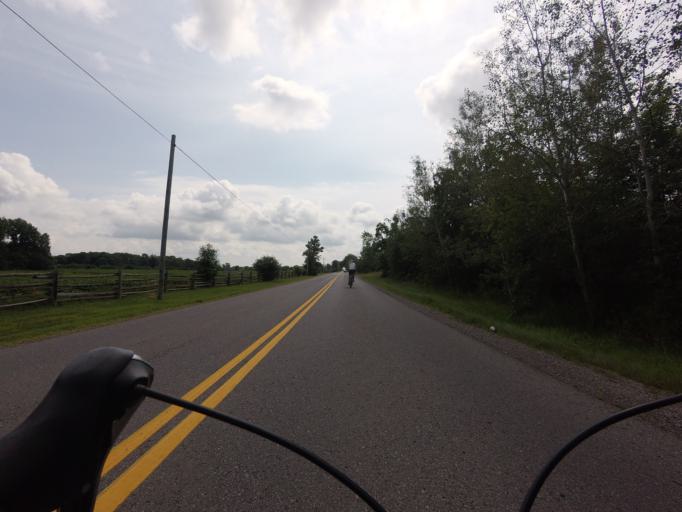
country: CA
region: Ontario
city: Brockville
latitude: 44.6171
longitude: -75.6567
